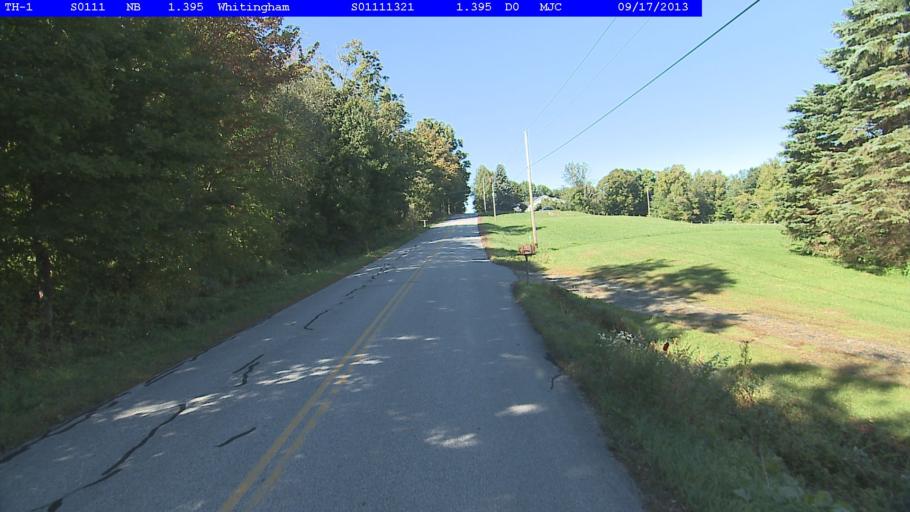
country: US
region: Massachusetts
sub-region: Franklin County
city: Charlemont
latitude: 42.7561
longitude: -72.8195
